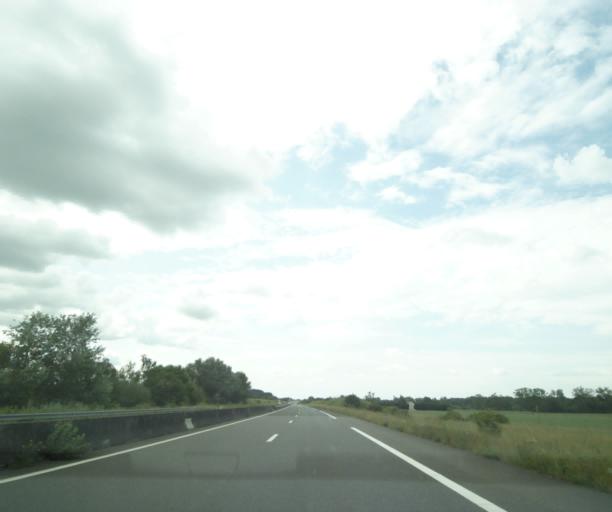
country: FR
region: Pays de la Loire
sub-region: Departement de Maine-et-Loire
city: Vivy
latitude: 47.3354
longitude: -0.0439
